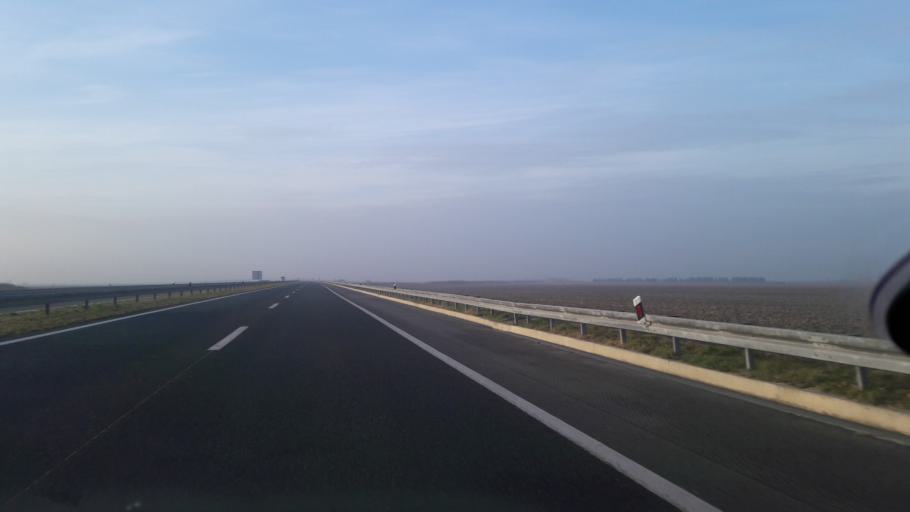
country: HR
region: Osjecko-Baranjska
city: Cepin
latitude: 45.5506
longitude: 18.5364
